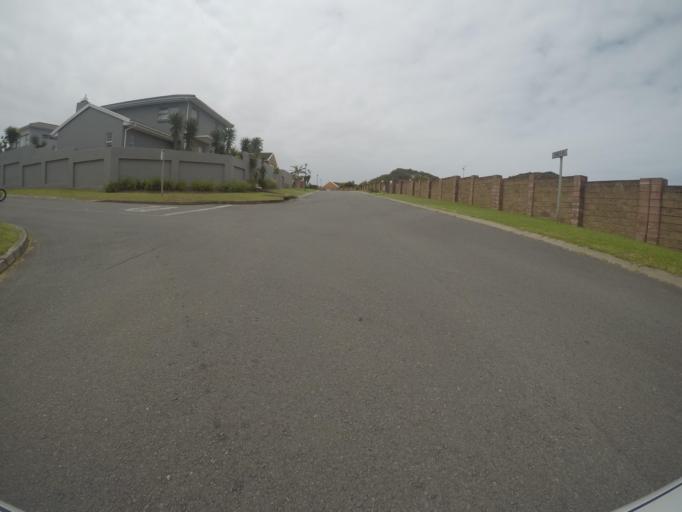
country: ZA
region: Eastern Cape
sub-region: Buffalo City Metropolitan Municipality
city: East London
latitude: -32.9795
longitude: 27.9545
